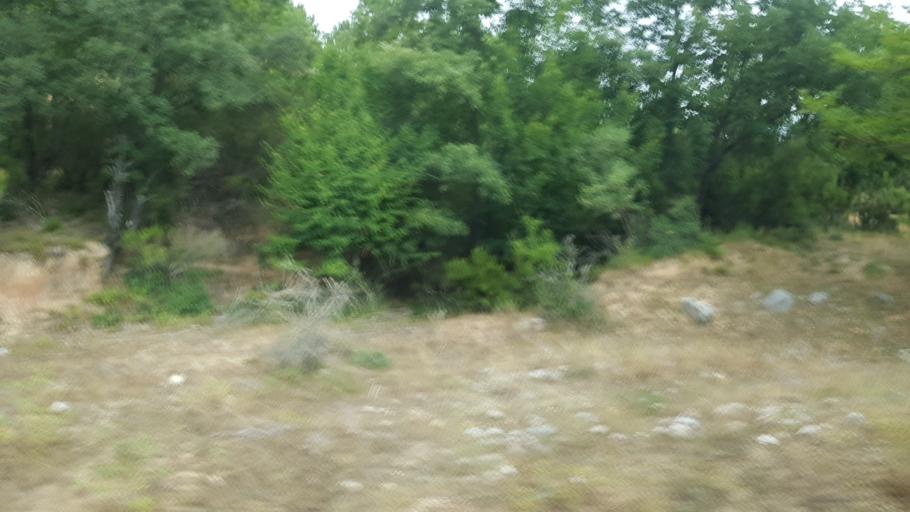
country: AL
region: Vlore
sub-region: Rrethi i Sarandes
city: Dhiver
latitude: 39.9120
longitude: 20.1874
